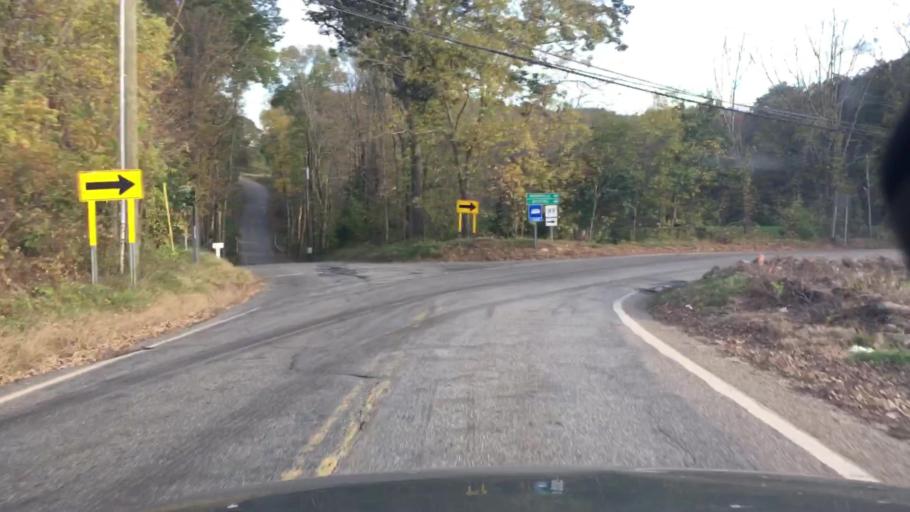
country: US
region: Connecticut
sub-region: Tolland County
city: Stafford
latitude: 41.9553
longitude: -72.1913
